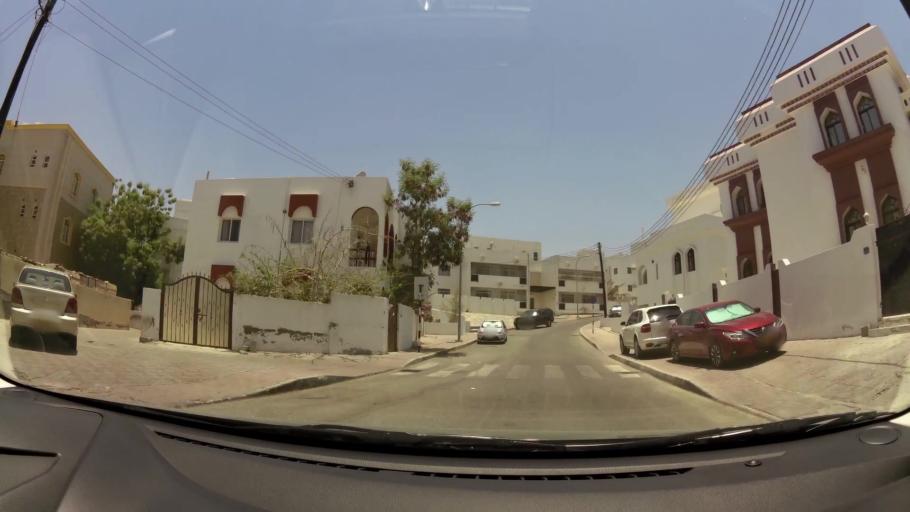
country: OM
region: Muhafazat Masqat
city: Muscat
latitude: 23.6166
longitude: 58.5393
